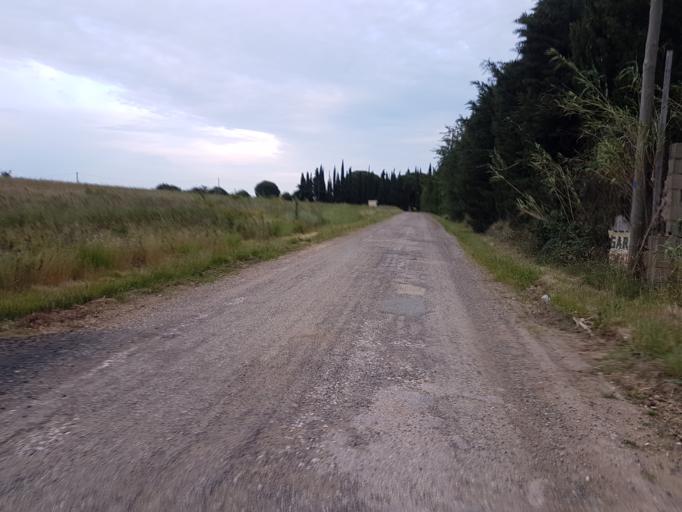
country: FR
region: Languedoc-Roussillon
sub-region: Departement de l'Herault
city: Portiragnes
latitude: 43.3148
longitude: 3.3416
